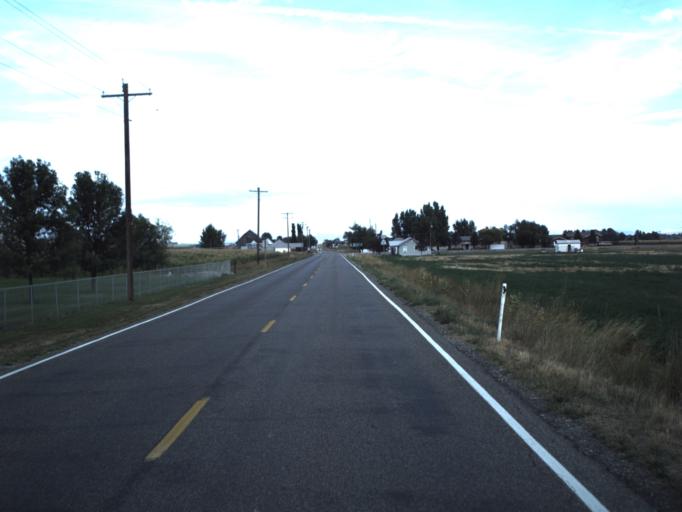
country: US
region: Utah
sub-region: Cache County
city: Lewiston
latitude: 41.9724
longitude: -111.9541
